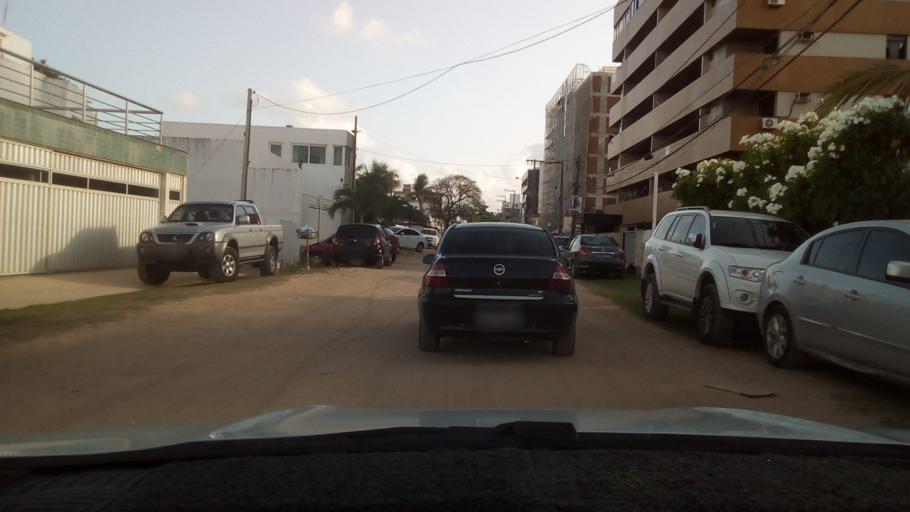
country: BR
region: Paraiba
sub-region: Cabedelo
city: Cabedelo
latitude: -7.0080
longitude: -34.8272
